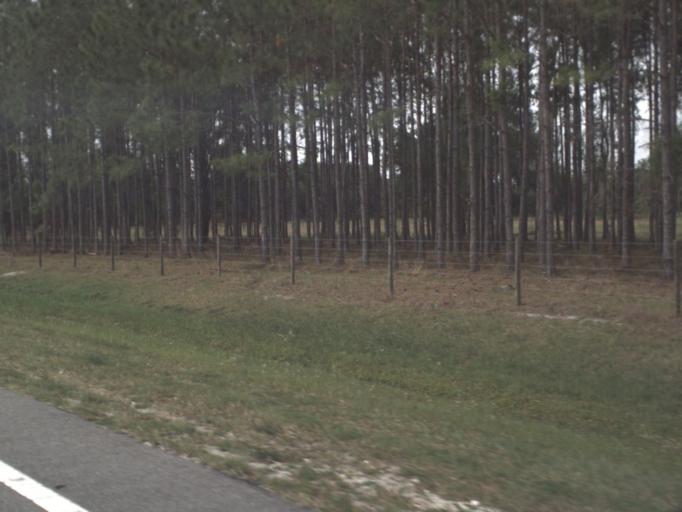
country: US
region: Florida
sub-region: Putnam County
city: Crescent City
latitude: 29.4904
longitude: -81.4710
